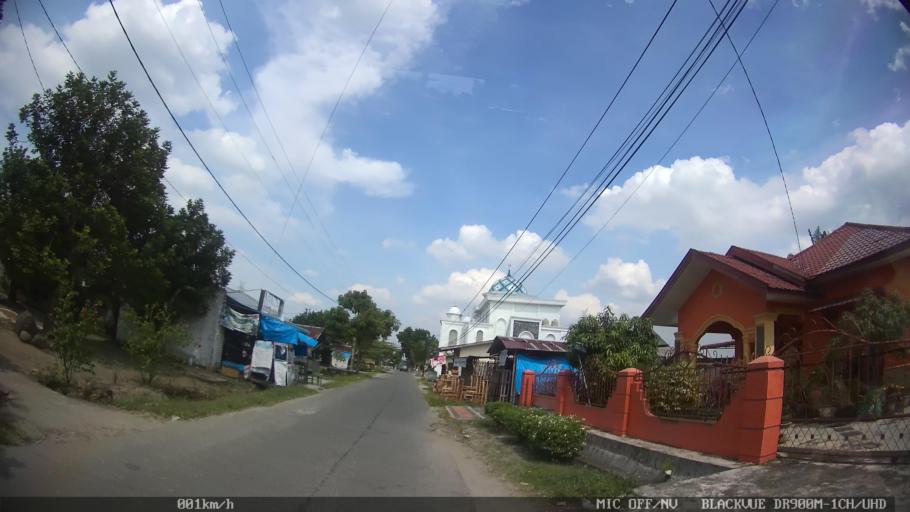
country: ID
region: North Sumatra
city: Binjai
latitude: 3.6353
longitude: 98.5021
